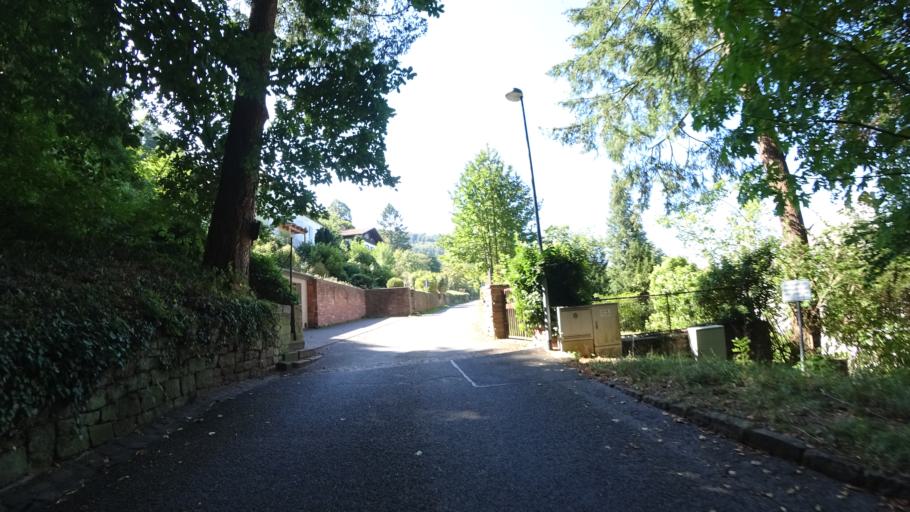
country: DE
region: Bavaria
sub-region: Regierungsbezirk Unterfranken
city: Miltenberg
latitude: 49.6979
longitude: 9.2566
